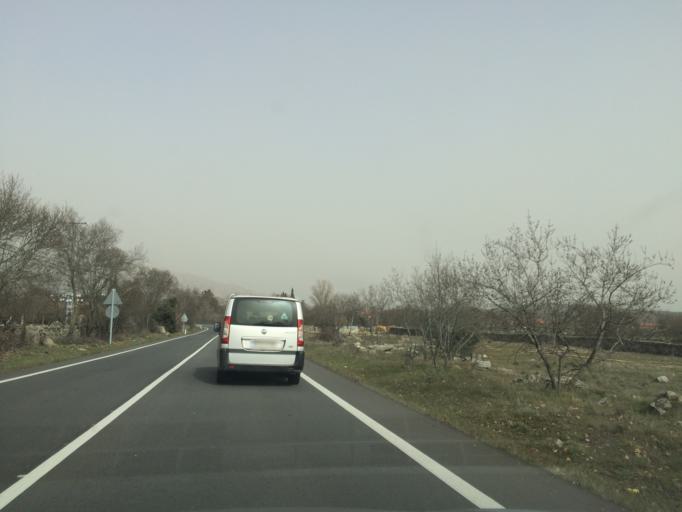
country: ES
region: Madrid
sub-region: Provincia de Madrid
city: Boalo
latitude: 40.6945
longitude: -3.9400
